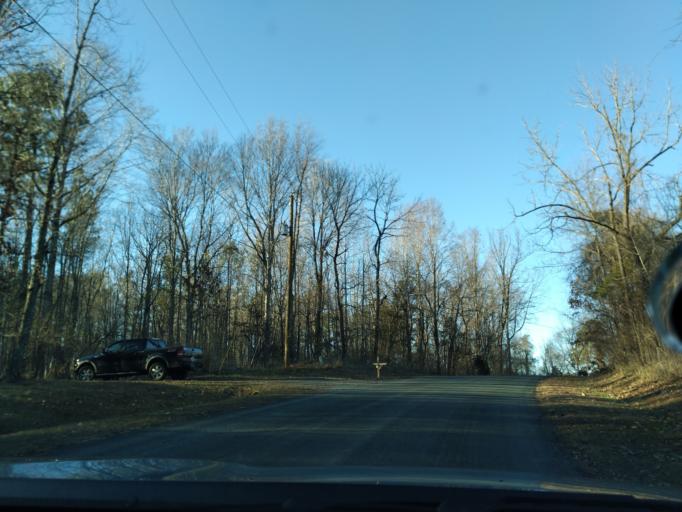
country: US
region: Virginia
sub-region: Buckingham County
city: Buckingham
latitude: 37.3924
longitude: -78.6452
